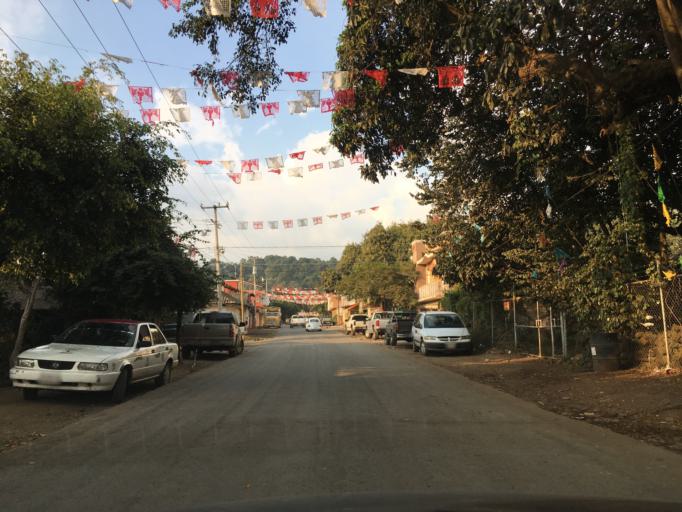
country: MX
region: Michoacan
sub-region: Ziracuaretiro
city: Patuan
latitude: 19.4473
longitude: -101.8872
